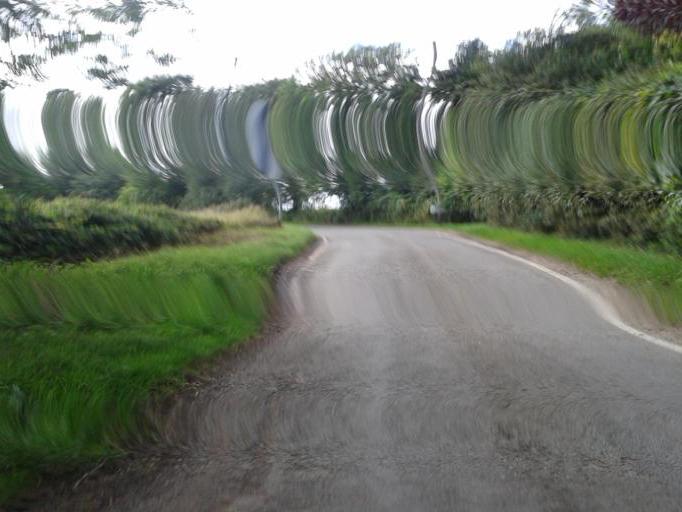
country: GB
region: England
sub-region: Cambridgeshire
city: Duxford
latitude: 51.9960
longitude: 0.1016
